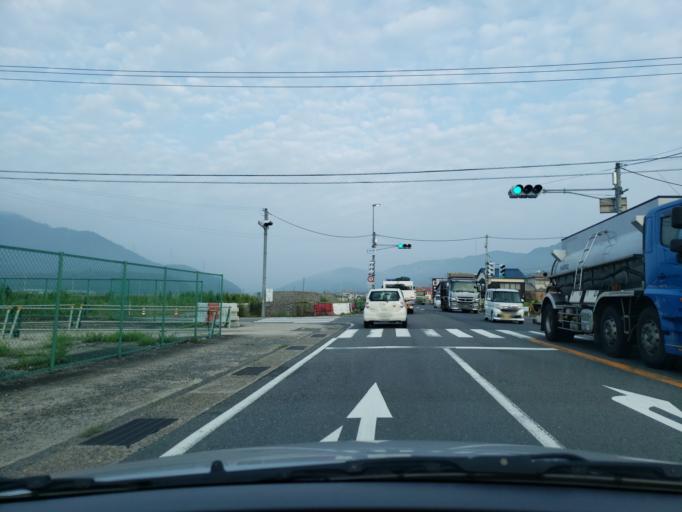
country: JP
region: Hyogo
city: Aioi
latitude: 34.8323
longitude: 134.4324
